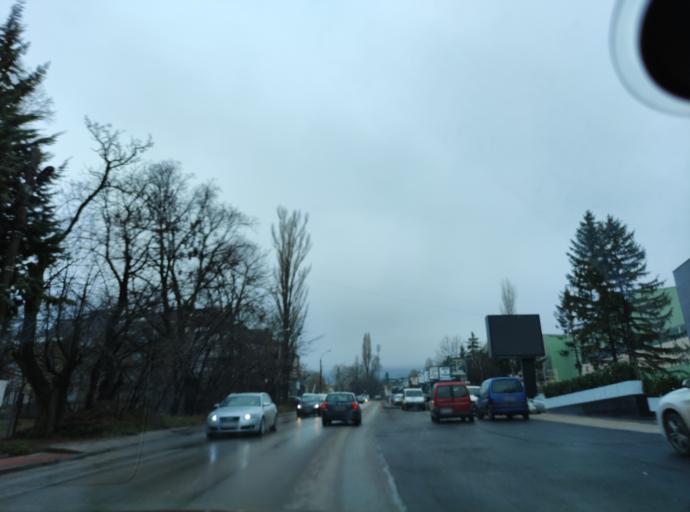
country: BG
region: Sofia-Capital
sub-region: Stolichna Obshtina
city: Sofia
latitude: 42.6384
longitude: 23.3115
